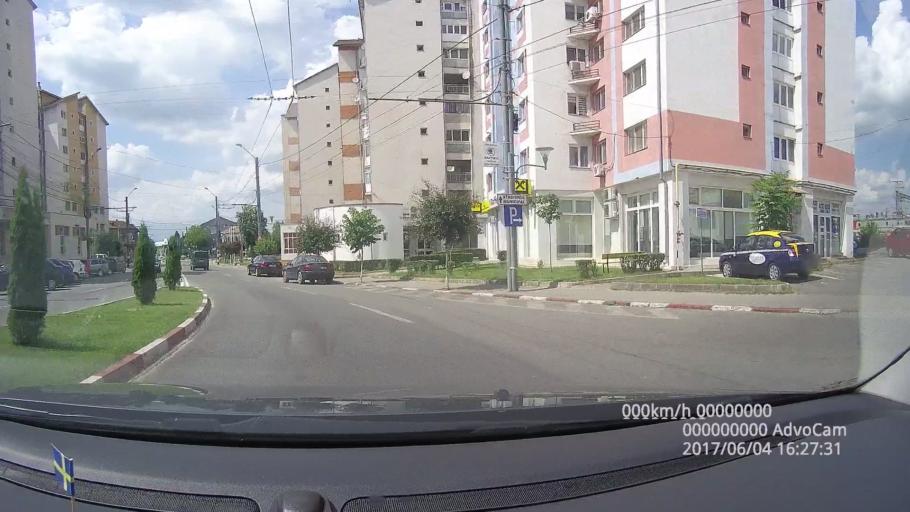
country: RO
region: Gorj
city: Targu Jiu
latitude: 45.0330
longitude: 23.2788
